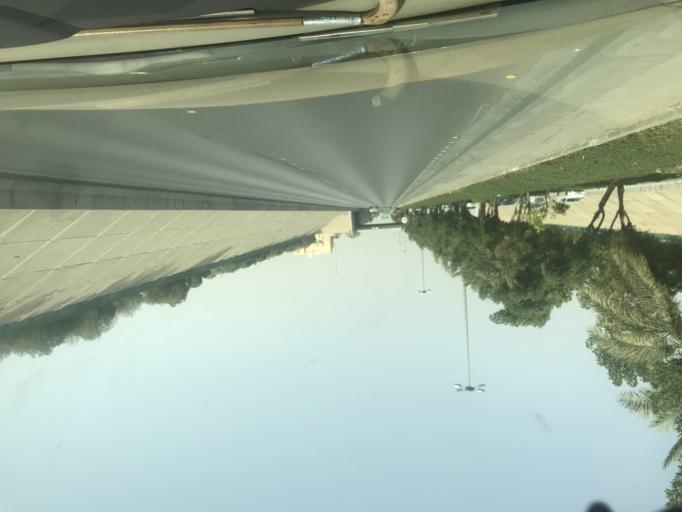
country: SA
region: Ar Riyad
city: Riyadh
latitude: 24.6673
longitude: 46.7918
